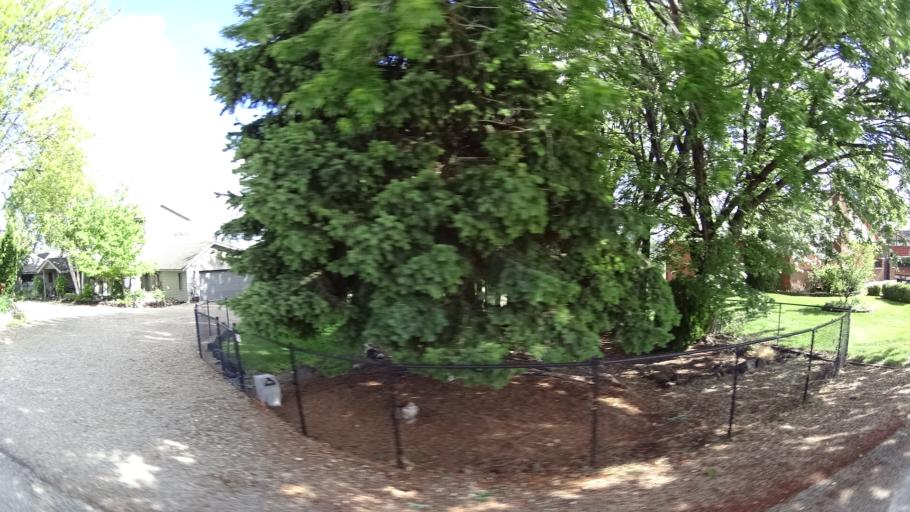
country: US
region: Idaho
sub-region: Ada County
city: Kuna
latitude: 43.4592
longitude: -116.4492
